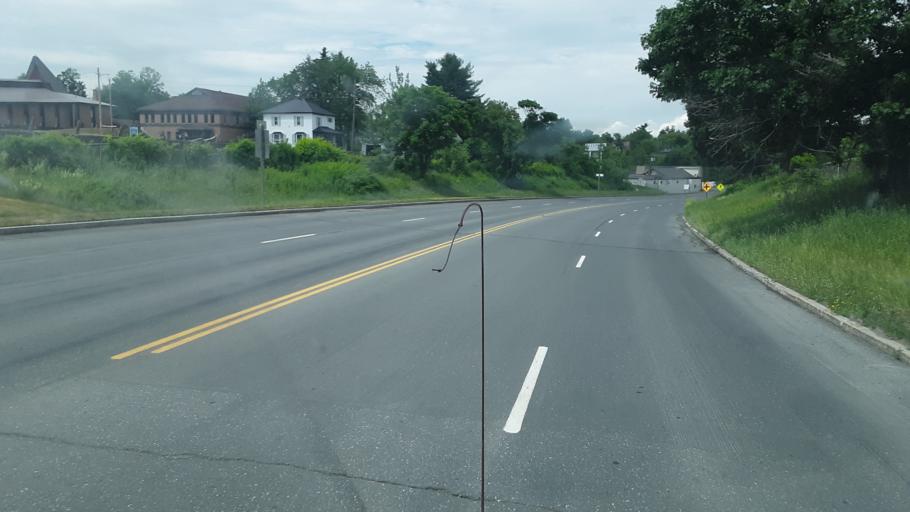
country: US
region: Maine
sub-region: Aroostook County
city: Caribou
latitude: 46.8546
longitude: -68.0060
